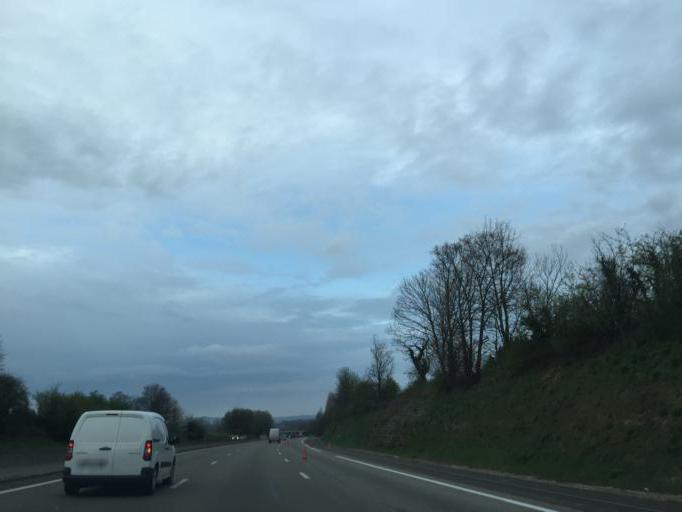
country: FR
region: Rhone-Alpes
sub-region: Departement de la Drome
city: Mercurol
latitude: 45.1170
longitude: 4.8931
